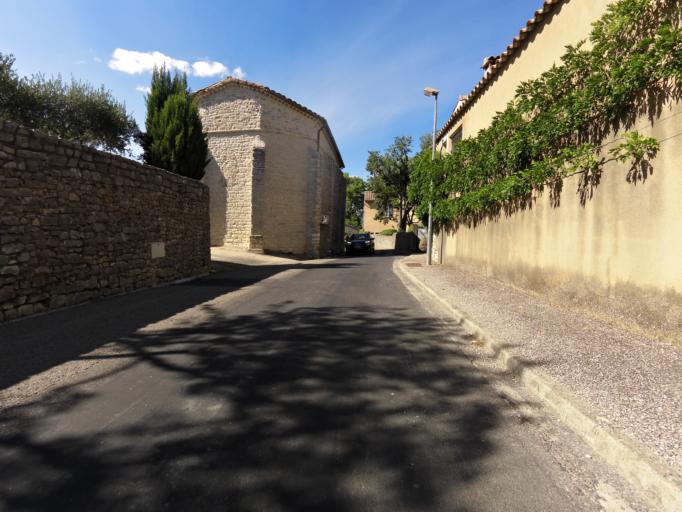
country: FR
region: Languedoc-Roussillon
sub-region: Departement du Gard
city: Quissac
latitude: 43.9563
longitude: 4.0296
